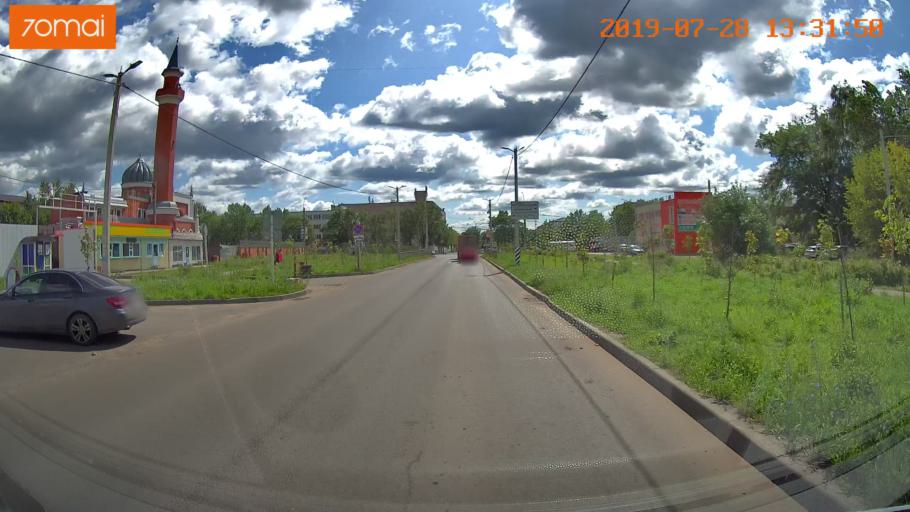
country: RU
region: Ivanovo
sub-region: Gorod Ivanovo
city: Ivanovo
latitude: 56.9650
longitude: 40.9844
